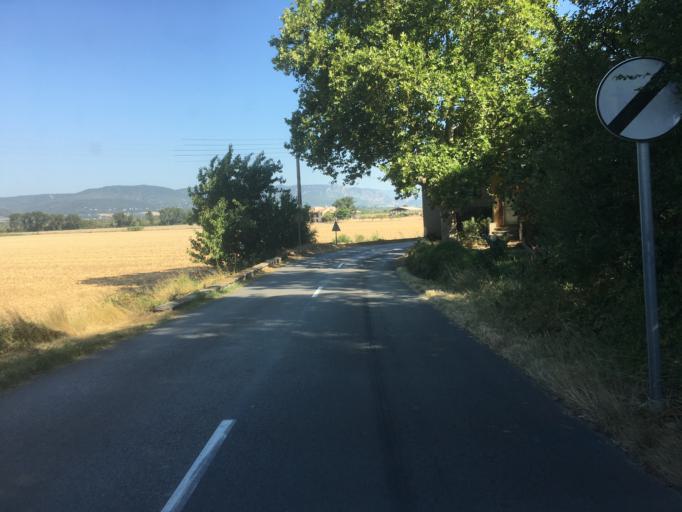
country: FR
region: Provence-Alpes-Cote d'Azur
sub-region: Departement des Alpes-de-Haute-Provence
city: Manosque
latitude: 43.8054
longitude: 5.8419
